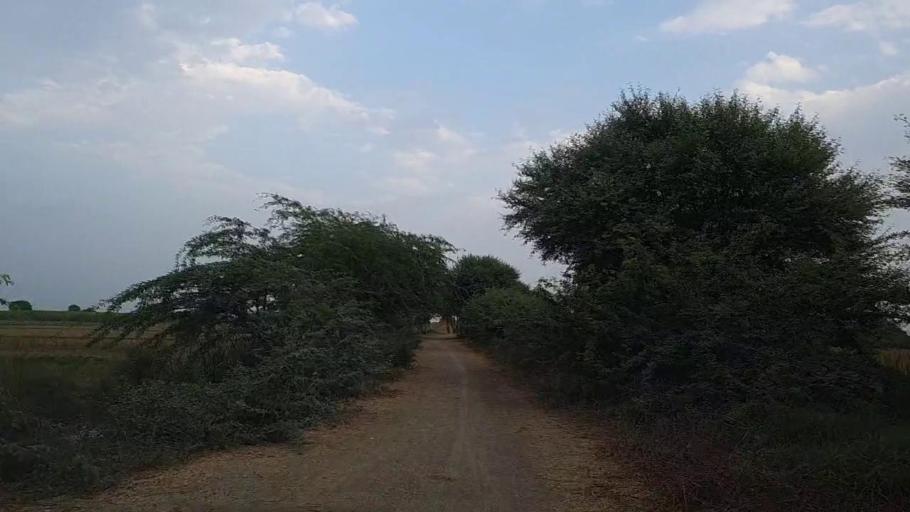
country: PK
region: Sindh
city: Daro Mehar
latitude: 24.7705
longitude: 68.1410
